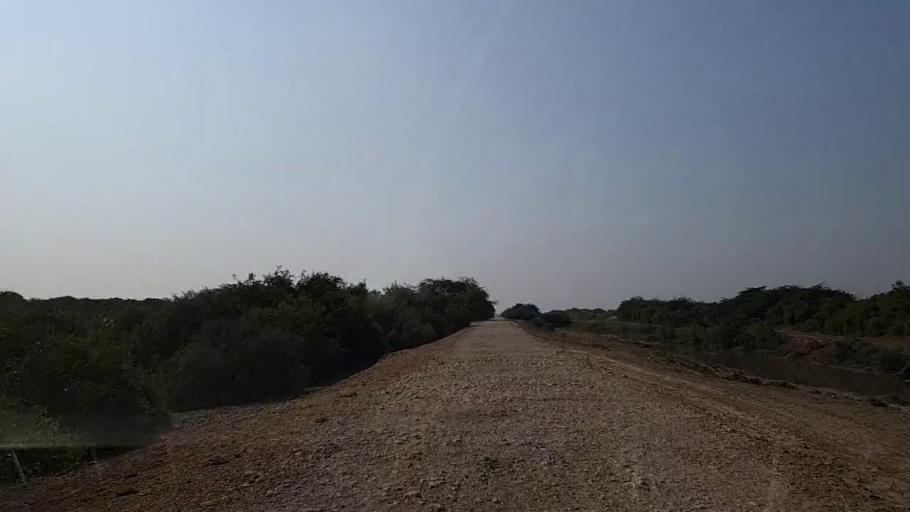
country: PK
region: Sindh
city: Mirpur Sakro
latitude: 24.6370
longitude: 67.7339
